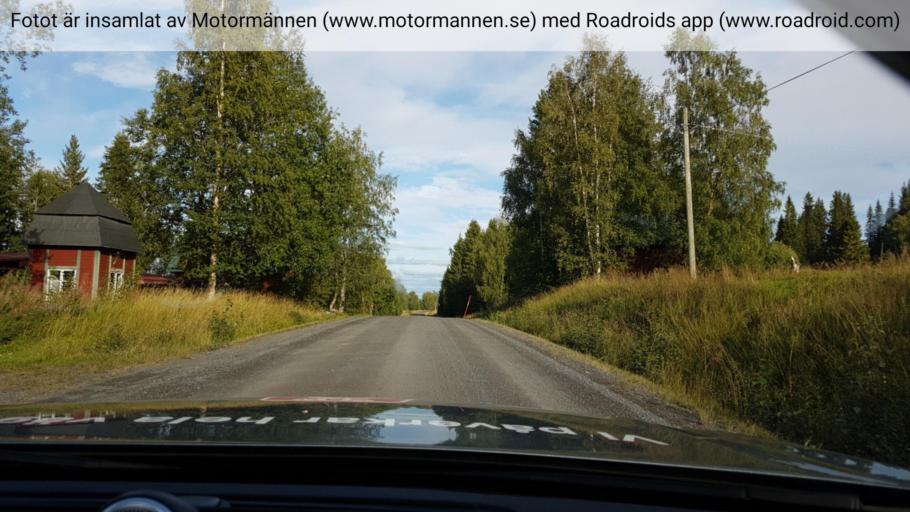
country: SE
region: Jaemtland
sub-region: Stroemsunds Kommun
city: Stroemsund
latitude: 64.1420
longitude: 15.7257
